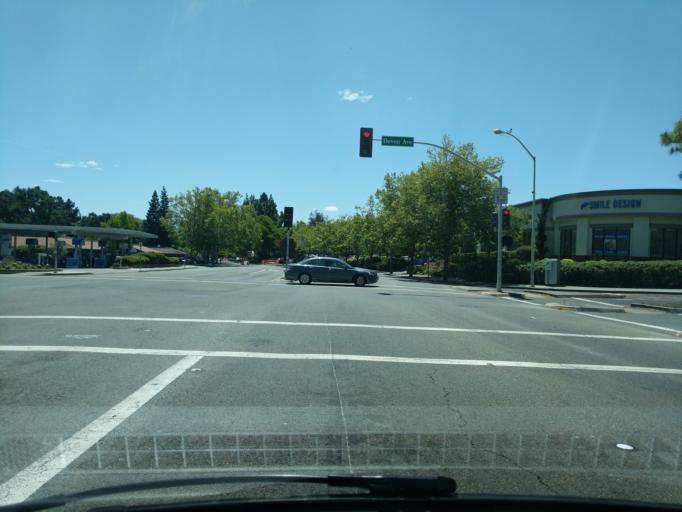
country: US
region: California
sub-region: Contra Costa County
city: Pleasant Hill
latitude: 37.9560
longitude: -122.0907
